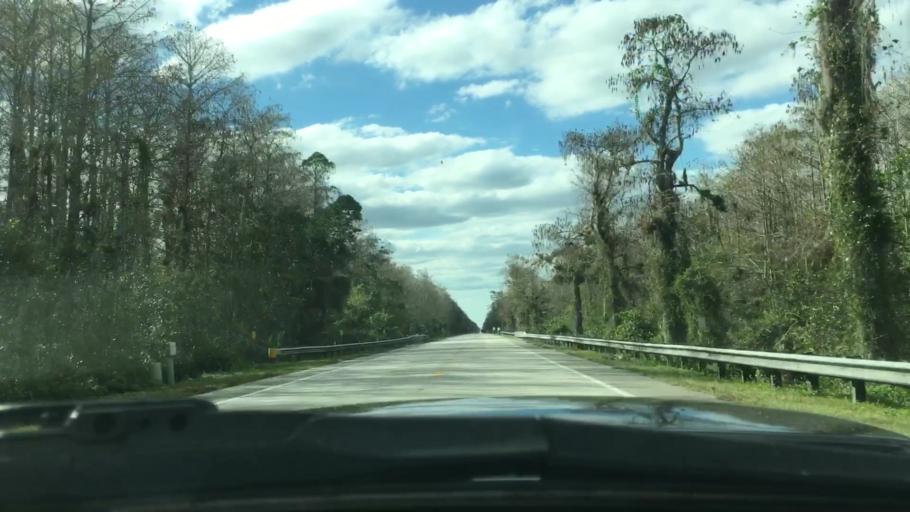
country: US
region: Florida
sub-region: Miami-Dade County
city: Kendall West
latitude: 25.8534
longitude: -81.0004
